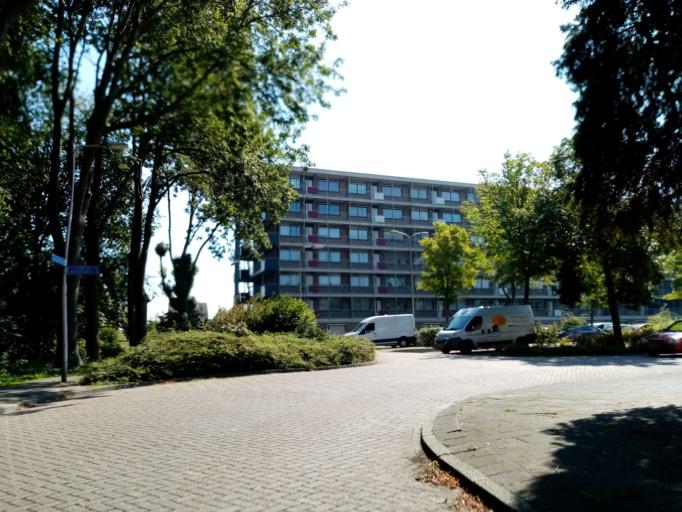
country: NL
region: South Holland
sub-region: Gemeente Lisse
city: Lisse
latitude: 52.2445
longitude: 4.5643
